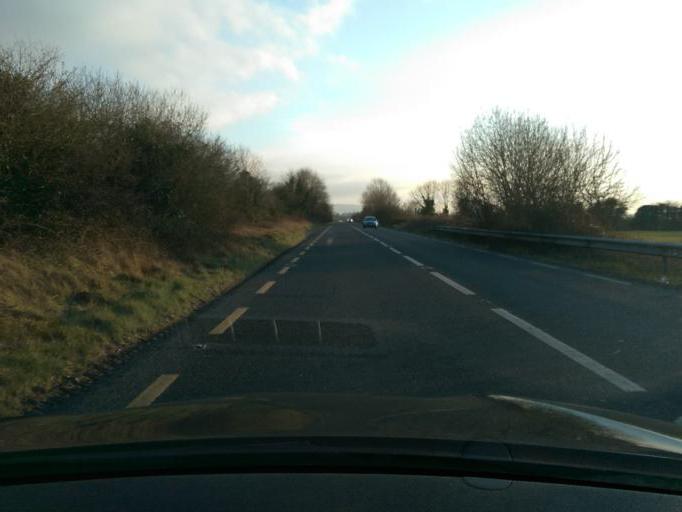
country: IE
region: Munster
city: Nenagh Bridge
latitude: 52.8896
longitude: -8.1904
